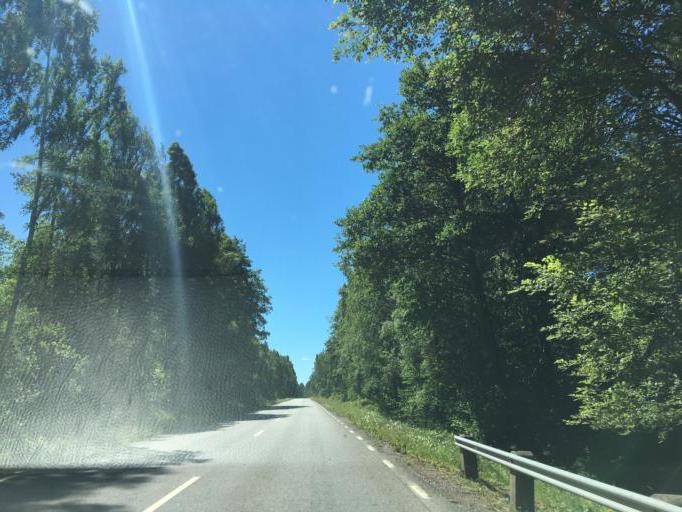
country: SE
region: OErebro
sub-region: Laxa Kommun
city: Laxa
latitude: 58.8324
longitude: 14.5462
